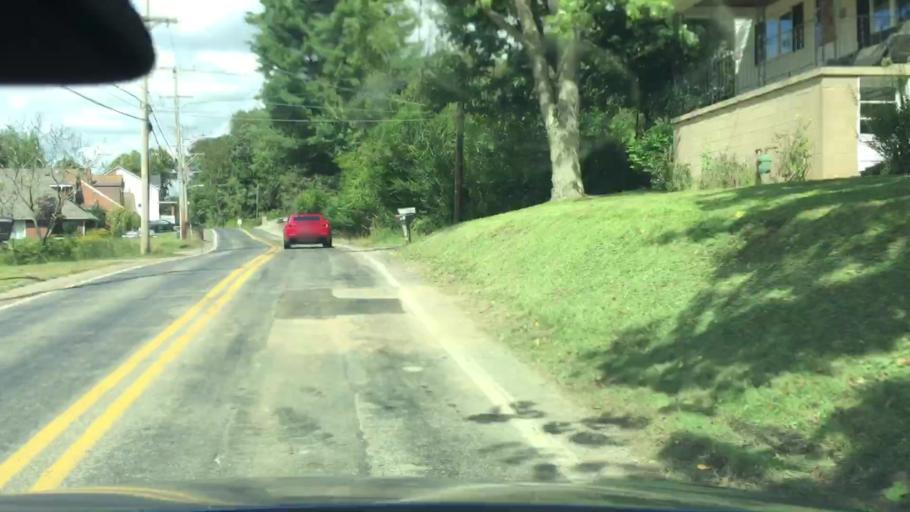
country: US
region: Pennsylvania
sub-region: Allegheny County
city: Russellton
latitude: 40.5786
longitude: -79.8236
